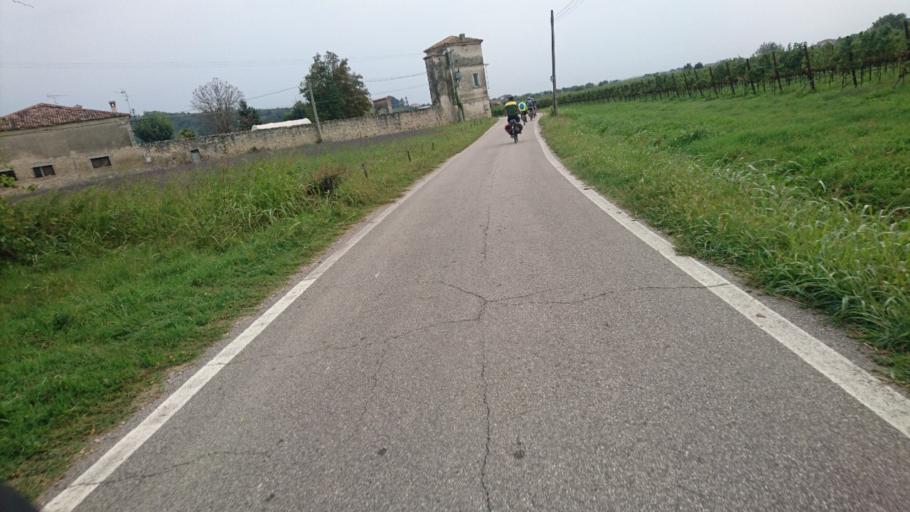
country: IT
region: Veneto
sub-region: Provincia di Verona
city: Colognola ai Colli
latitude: 45.4208
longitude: 11.2046
